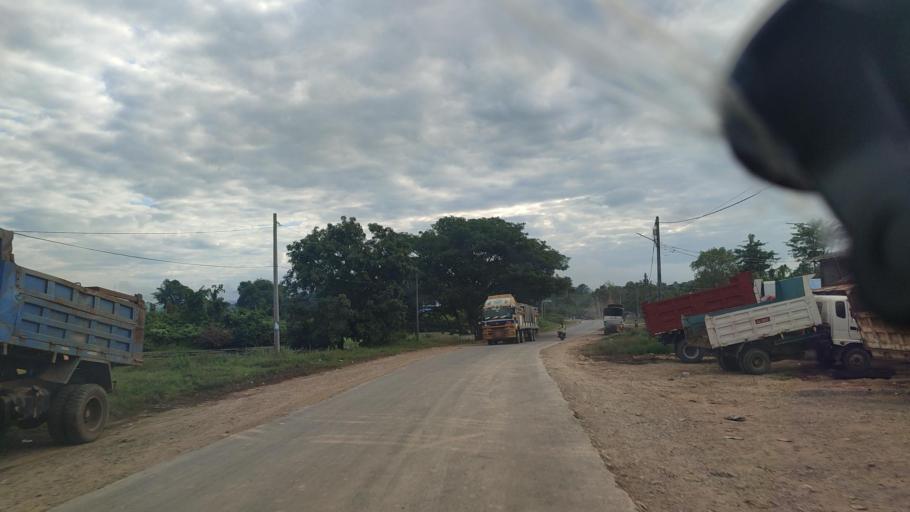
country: MM
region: Magway
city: Minbu
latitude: 19.7634
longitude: 94.0320
